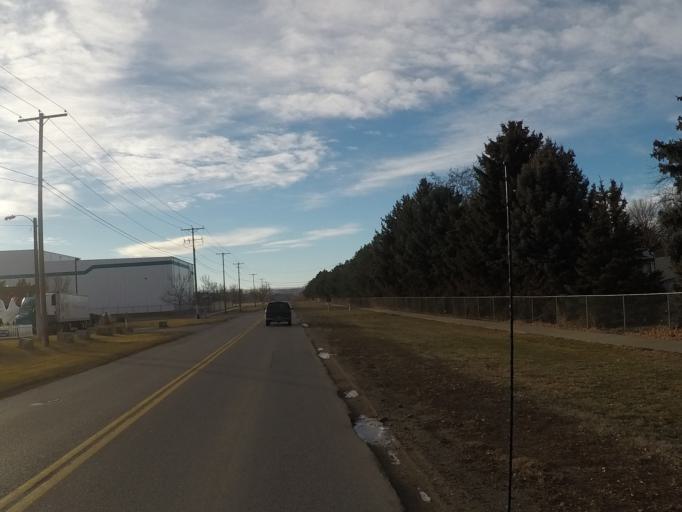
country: US
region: Montana
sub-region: Yellowstone County
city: Billings
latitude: 45.7523
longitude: -108.5969
